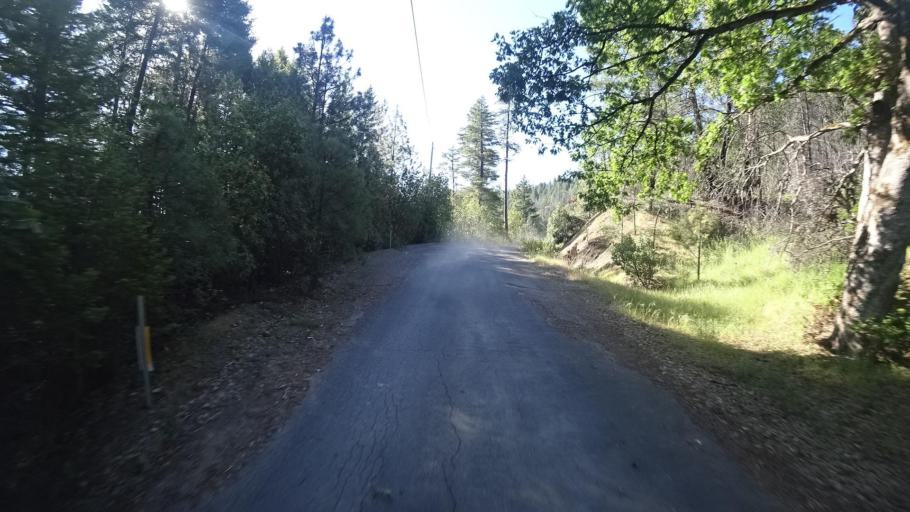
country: US
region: California
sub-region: Lake County
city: Upper Lake
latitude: 39.4056
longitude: -122.9722
